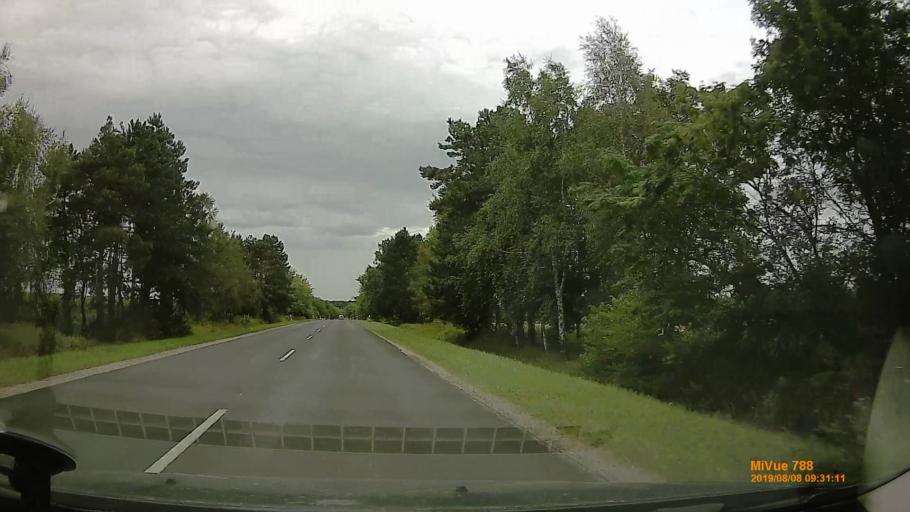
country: HU
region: Vas
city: Vasvar
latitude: 46.9939
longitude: 16.8302
